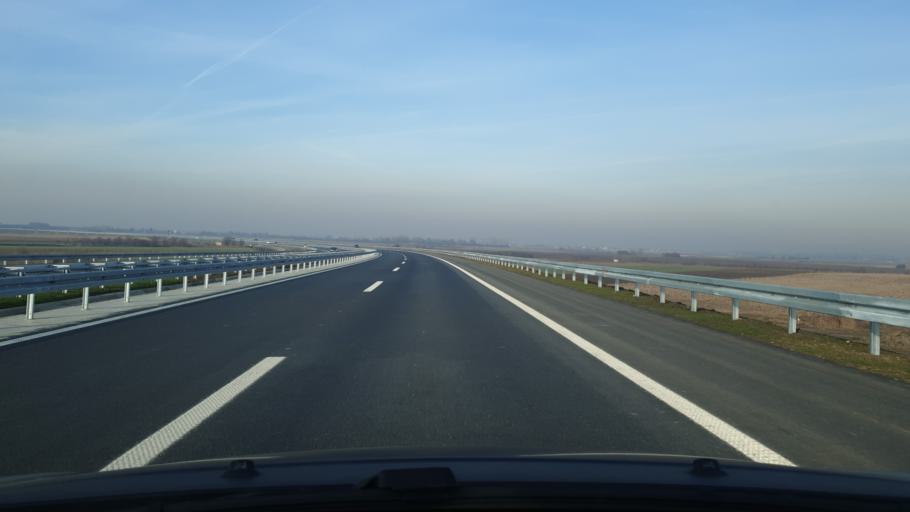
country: RS
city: Boljevci
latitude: 44.7191
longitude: 20.2583
